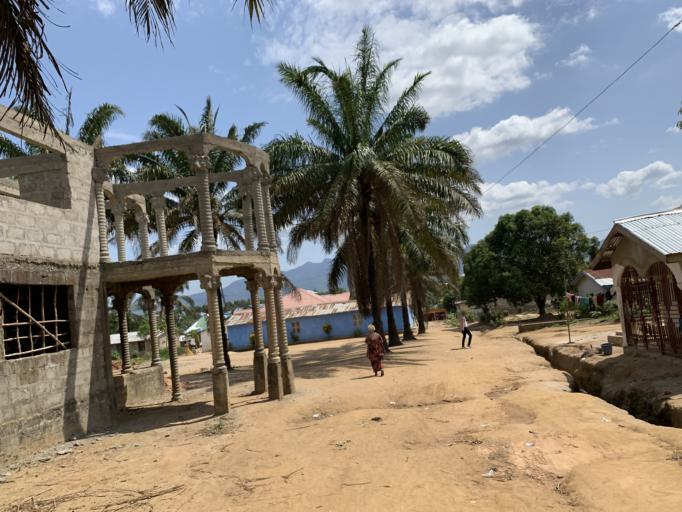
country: SL
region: Western Area
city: Waterloo
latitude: 8.3293
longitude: -13.0448
